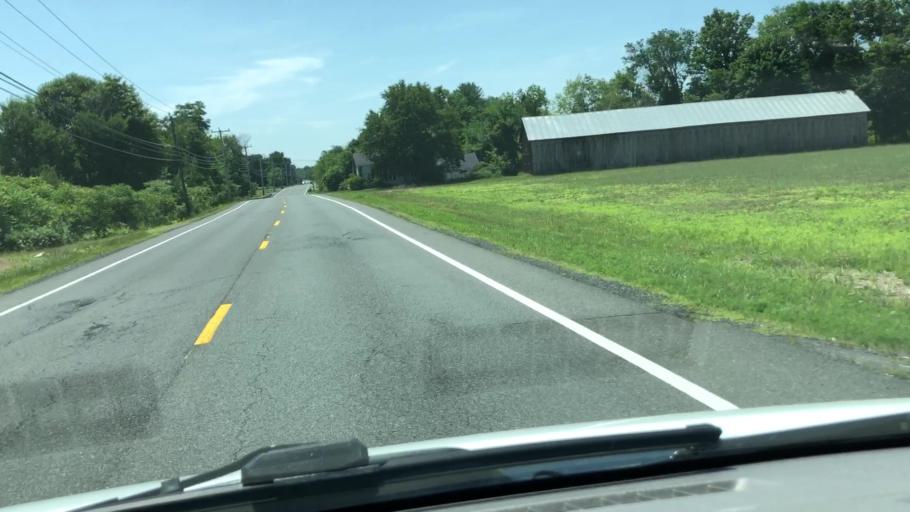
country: US
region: Massachusetts
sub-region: Franklin County
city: Whately
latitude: 42.4417
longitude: -72.6251
